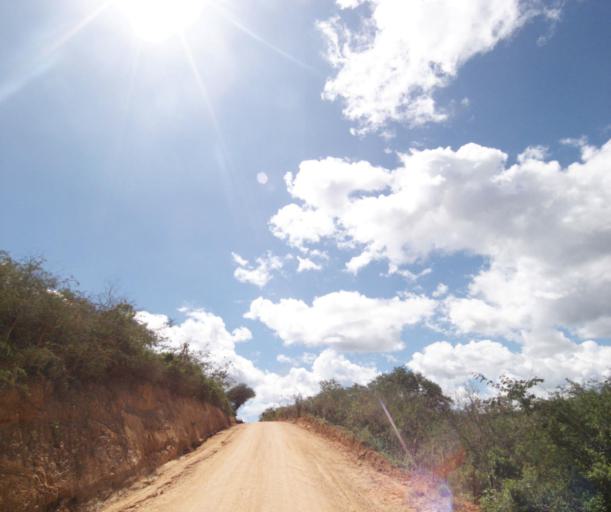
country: BR
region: Bahia
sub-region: Pocoes
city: Pocoes
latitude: -14.2998
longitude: -40.6421
